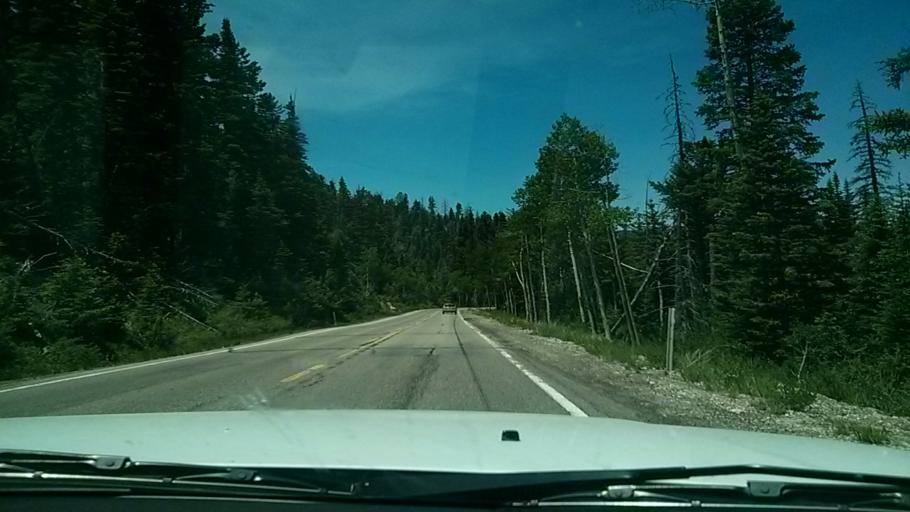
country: US
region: Utah
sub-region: Iron County
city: Cedar City
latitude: 37.5905
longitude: -112.8994
